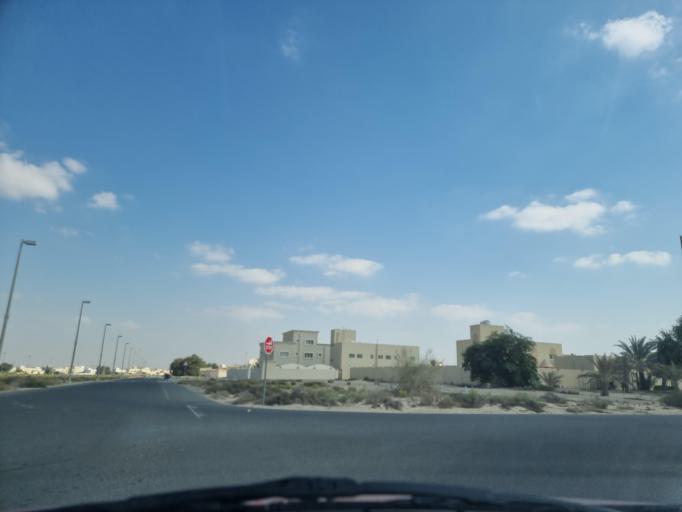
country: AE
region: Abu Dhabi
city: Abu Dhabi
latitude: 24.4032
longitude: 54.7400
